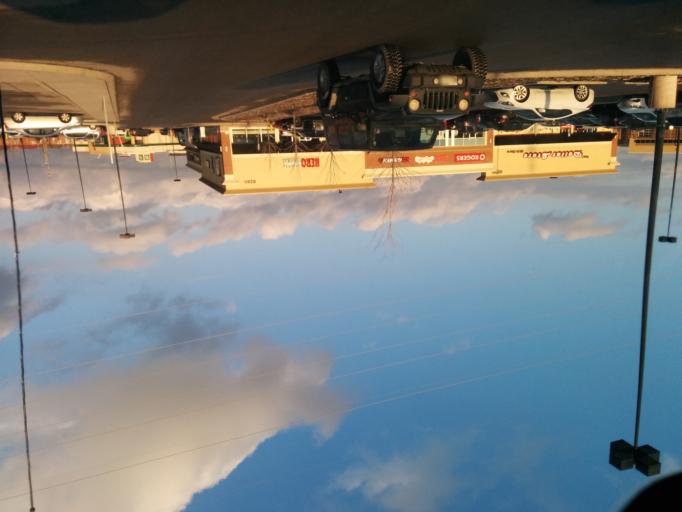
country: CA
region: Ontario
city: Vaughan
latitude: 43.7840
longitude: -79.6266
